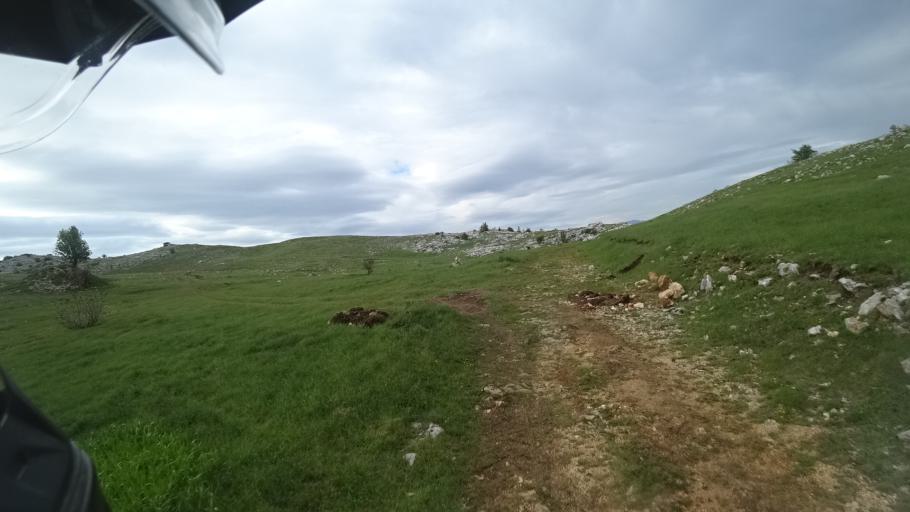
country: HR
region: Sibensko-Kniniska
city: Drnis
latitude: 43.8593
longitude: 16.3795
